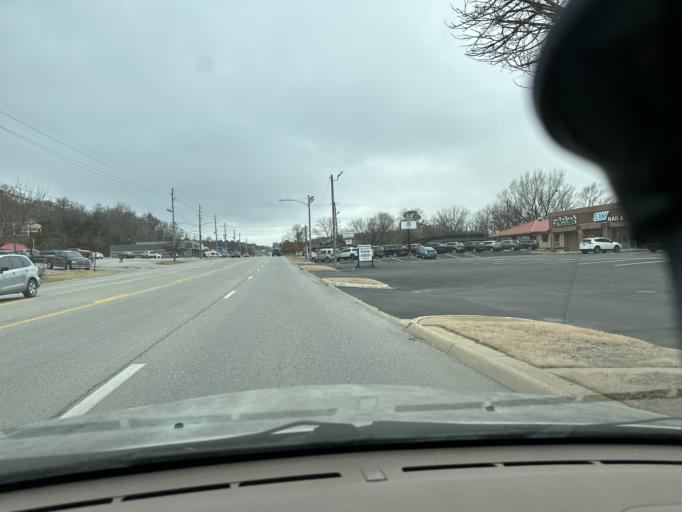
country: US
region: Arkansas
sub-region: Washington County
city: Fayetteville
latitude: 36.0941
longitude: -94.1531
